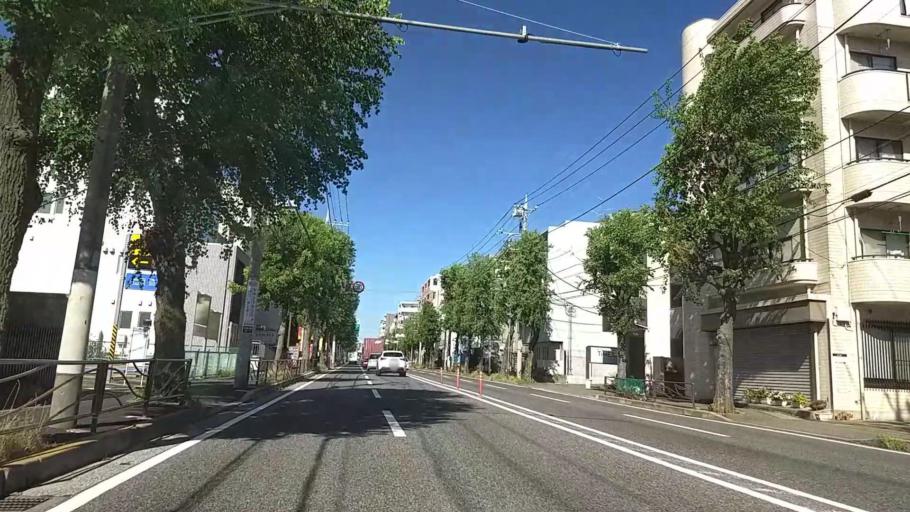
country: JP
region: Tokyo
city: Chofugaoka
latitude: 35.5834
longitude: 139.5874
